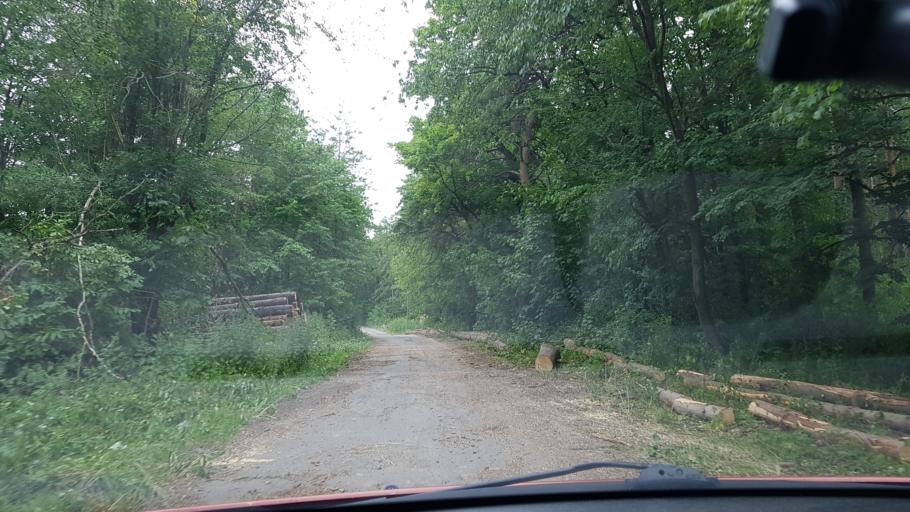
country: PL
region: Lower Silesian Voivodeship
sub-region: Powiat zabkowicki
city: Stoszowice
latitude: 50.5581
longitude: 16.7598
